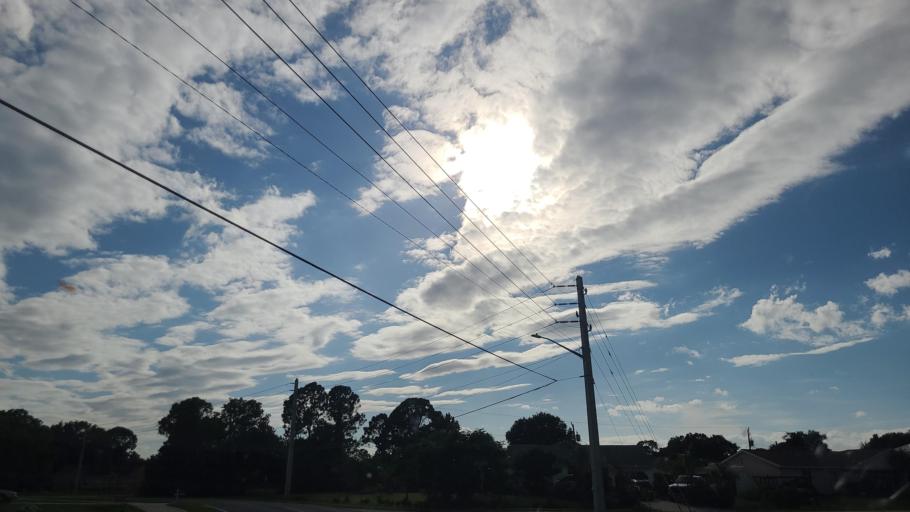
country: US
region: Florida
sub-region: Brevard County
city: June Park
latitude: 28.0116
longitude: -80.6842
